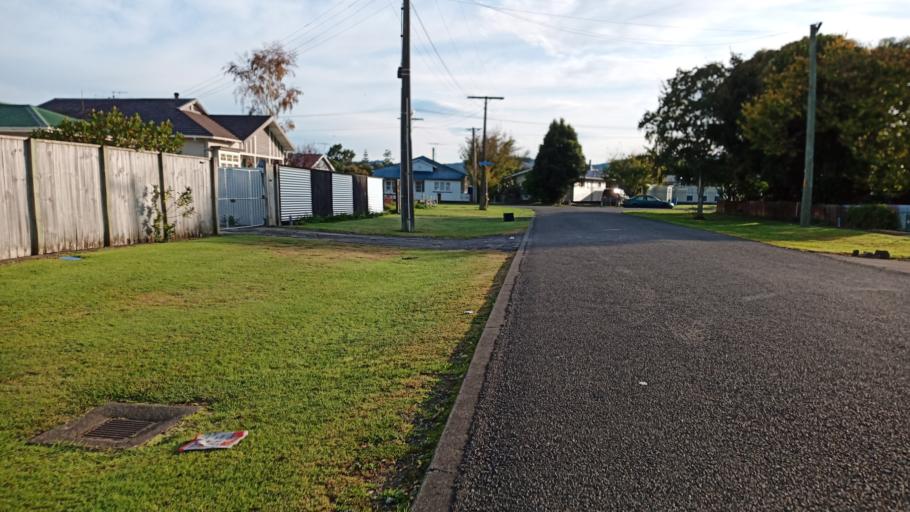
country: NZ
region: Gisborne
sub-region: Gisborne District
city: Gisborne
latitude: -38.6585
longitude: 178.0060
